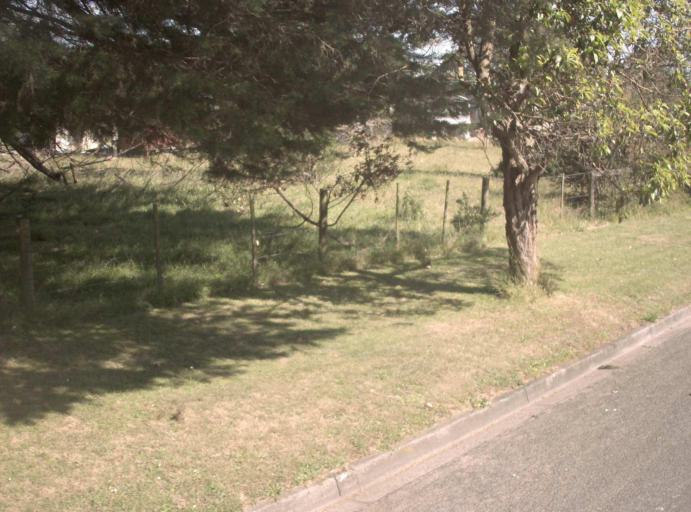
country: AU
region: Victoria
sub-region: Baw Baw
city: Warragul
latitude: -38.3395
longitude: 145.7654
